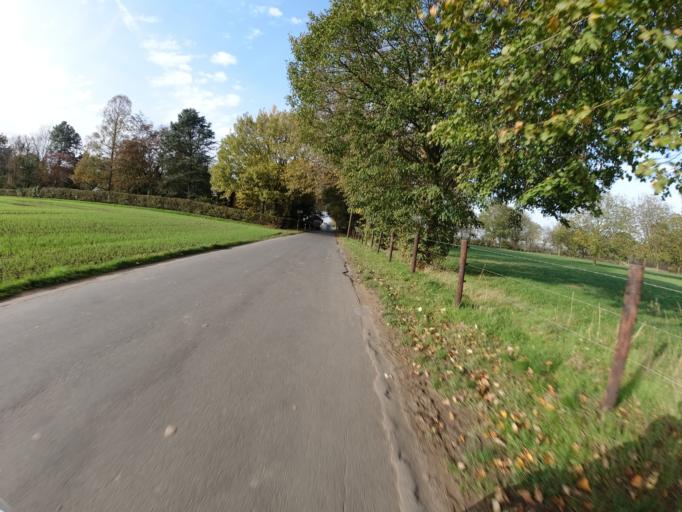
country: DE
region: North Rhine-Westphalia
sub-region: Regierungsbezirk Dusseldorf
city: Moers
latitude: 51.4133
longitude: 6.6251
